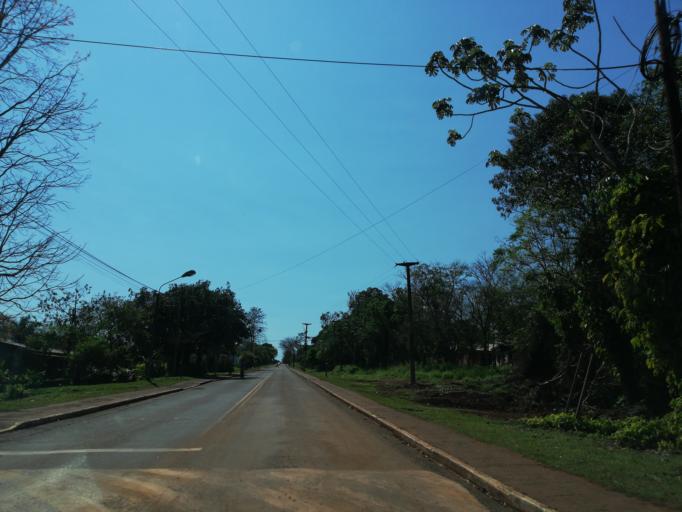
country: AR
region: Misiones
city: Puerto Eldorado
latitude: -26.4119
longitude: -54.6850
